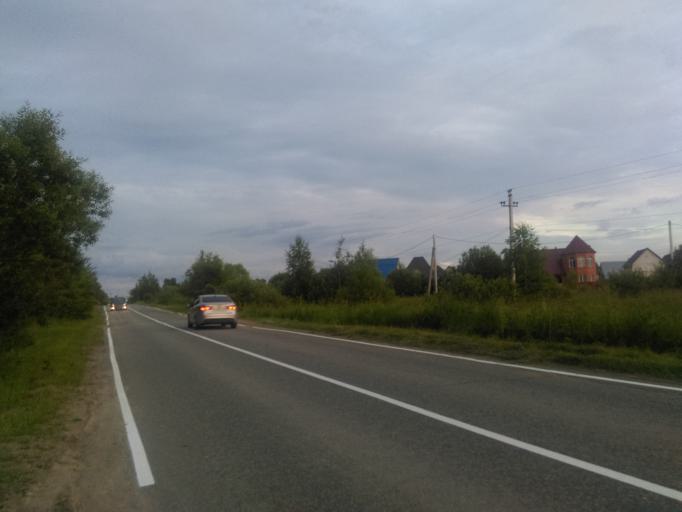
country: RU
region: Moskovskaya
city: Vostryakovo
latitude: 55.3883
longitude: 37.8093
